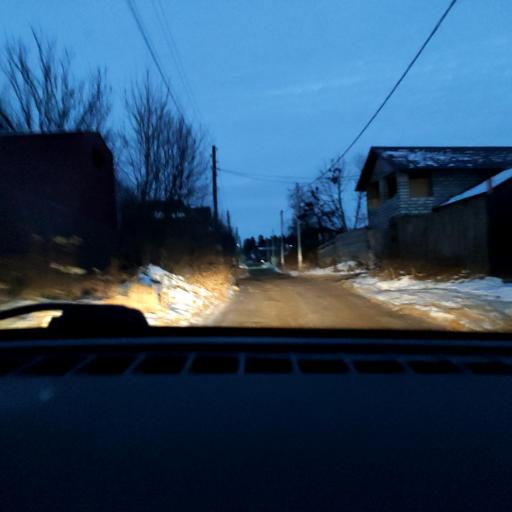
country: RU
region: Perm
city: Kondratovo
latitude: 57.9562
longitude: 56.1541
